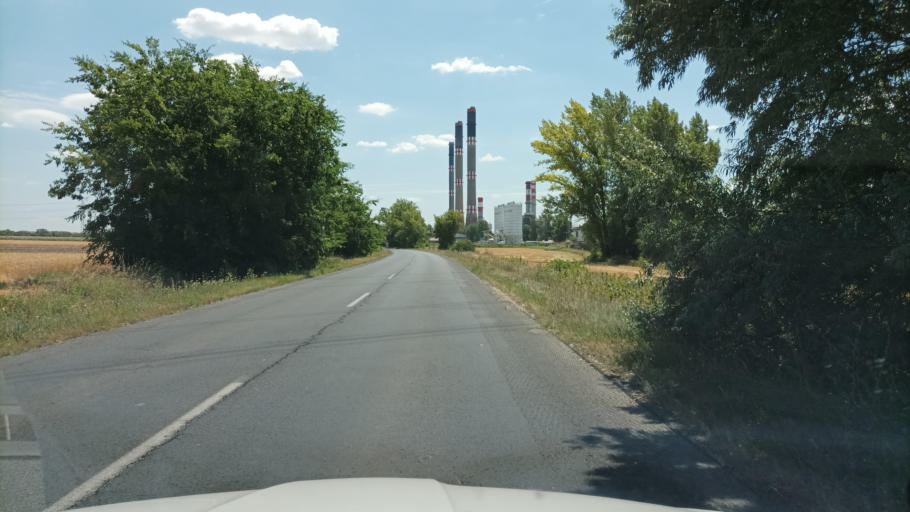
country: HU
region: Pest
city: Szazhalombatta
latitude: 47.3374
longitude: 18.9119
